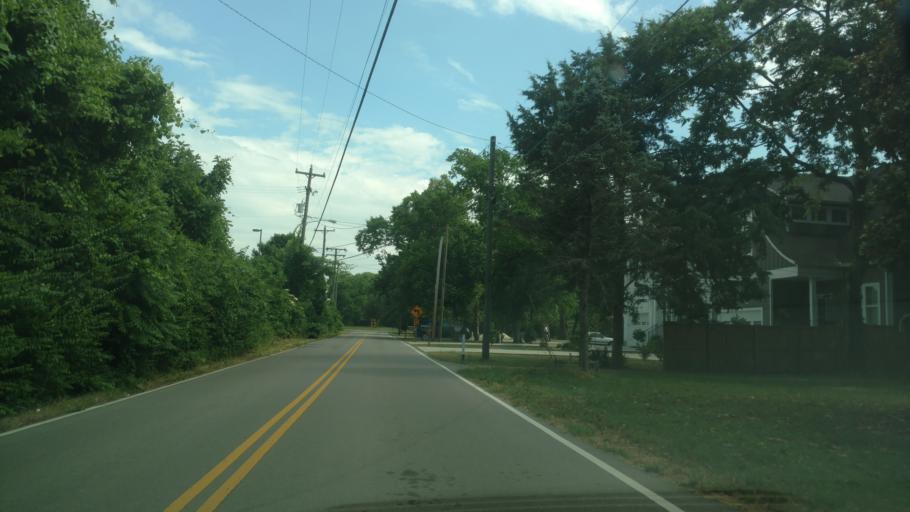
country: US
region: Tennessee
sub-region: Davidson County
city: Lakewood
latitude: 36.2190
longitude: -86.7052
